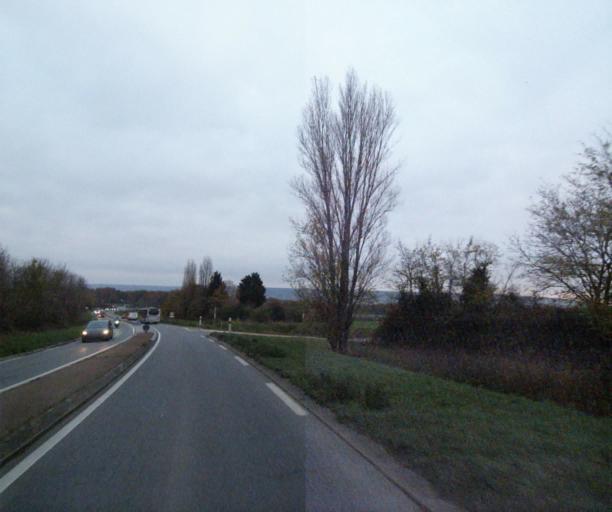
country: FR
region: Ile-de-France
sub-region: Departement des Yvelines
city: Medan
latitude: 48.9549
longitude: 1.9805
